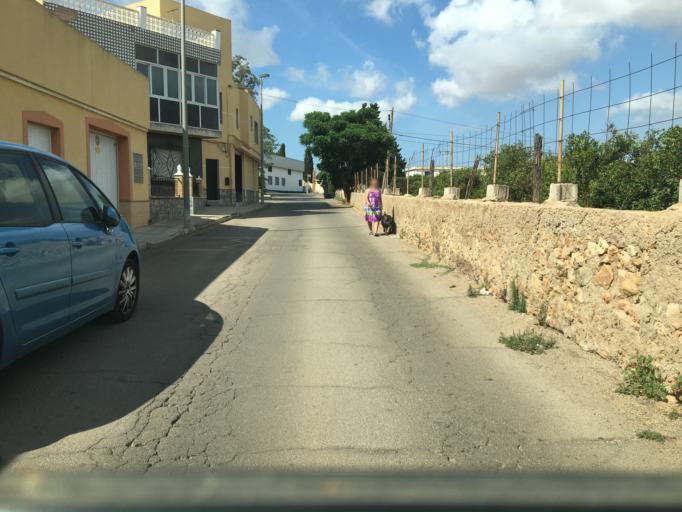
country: ES
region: Murcia
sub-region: Murcia
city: La Union
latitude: 37.6452
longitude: -0.8713
